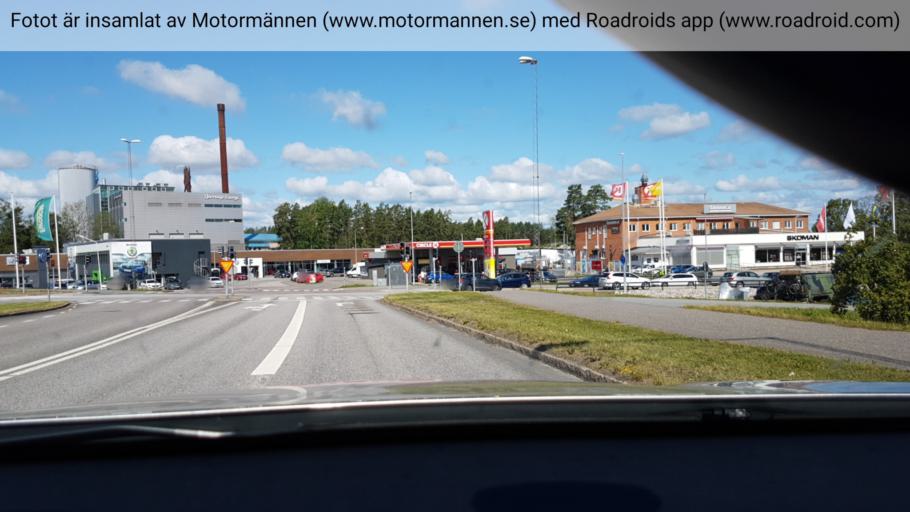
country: SE
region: Stockholm
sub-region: Norrtalje Kommun
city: Norrtalje
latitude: 59.7501
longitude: 18.6898
